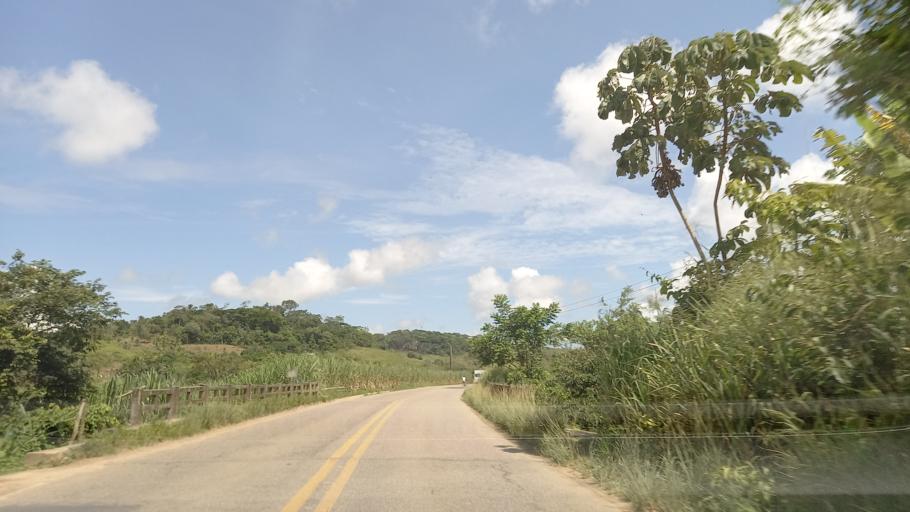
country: BR
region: Pernambuco
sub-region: Barreiros
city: Barreiros
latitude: -8.7749
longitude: -35.1734
